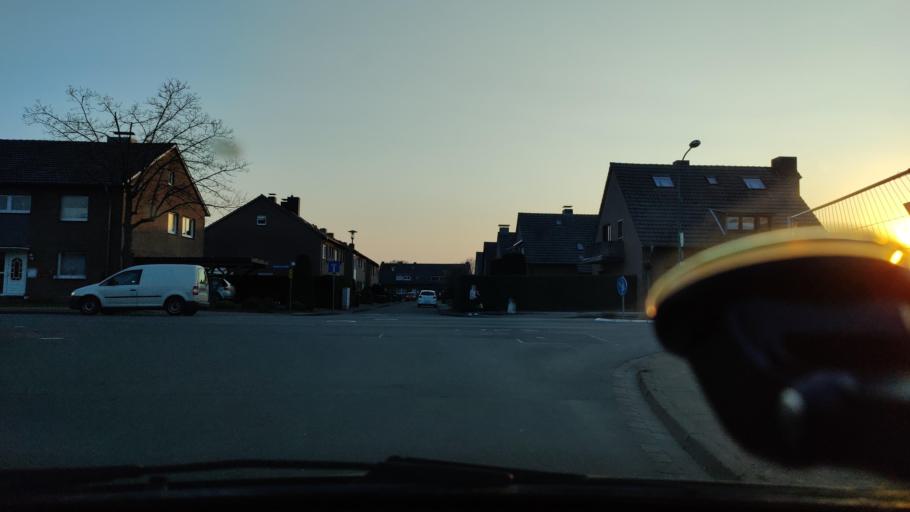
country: DE
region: North Rhine-Westphalia
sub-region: Regierungsbezirk Dusseldorf
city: Weeze
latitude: 51.6212
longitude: 6.2075
